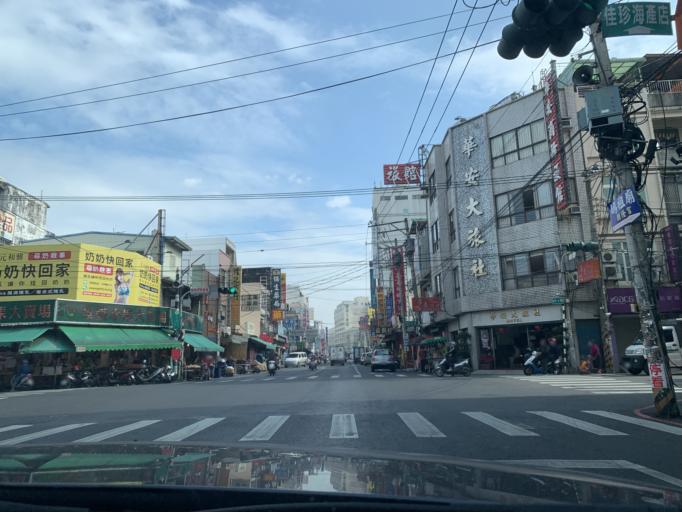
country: TW
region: Taiwan
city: Fengshan
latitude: 22.4670
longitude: 120.4497
